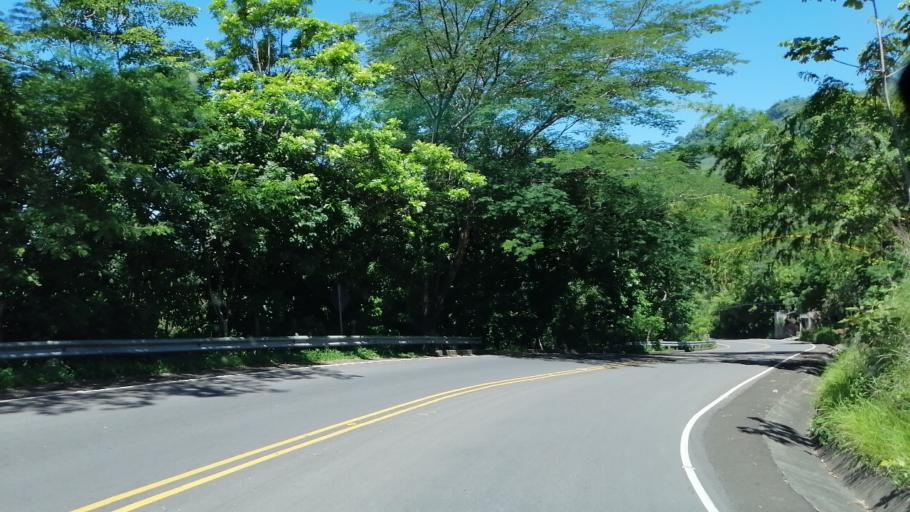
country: SV
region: San Miguel
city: Ciudad Barrios
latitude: 13.8156
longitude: -88.1858
